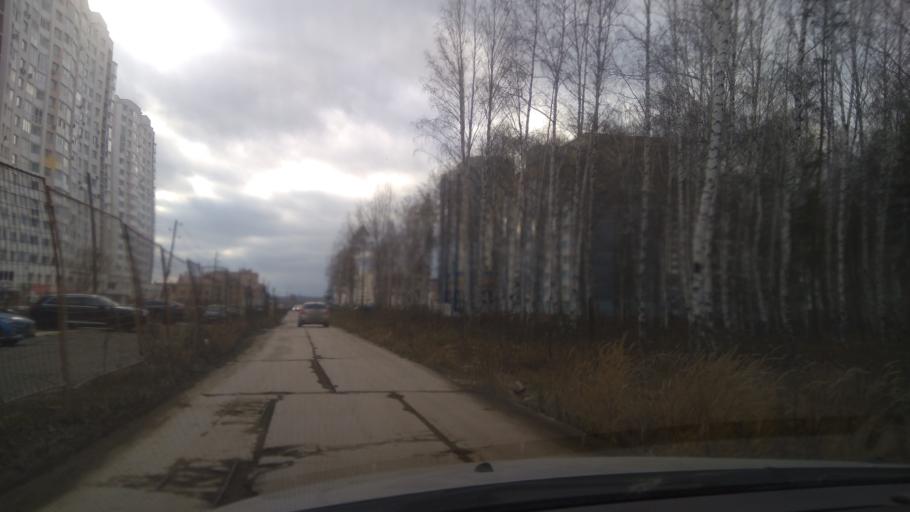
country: RU
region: Sverdlovsk
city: Sovkhoznyy
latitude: 56.7850
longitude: 60.5430
